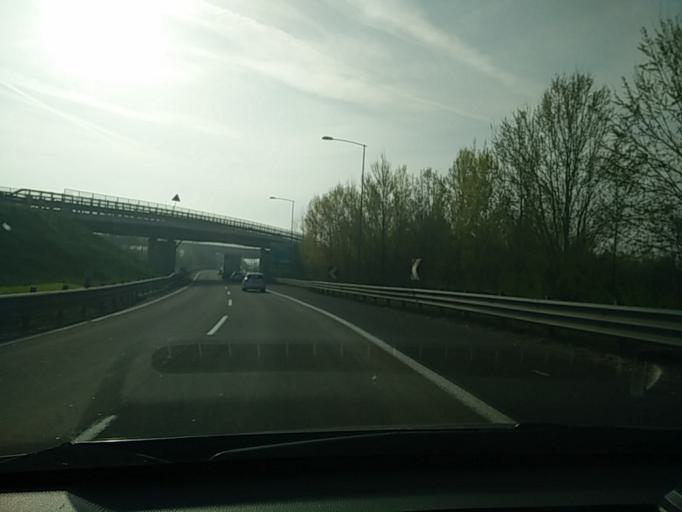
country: IT
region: Emilia-Romagna
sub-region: Provincia di Bologna
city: Bologna
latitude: 44.5197
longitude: 11.3691
